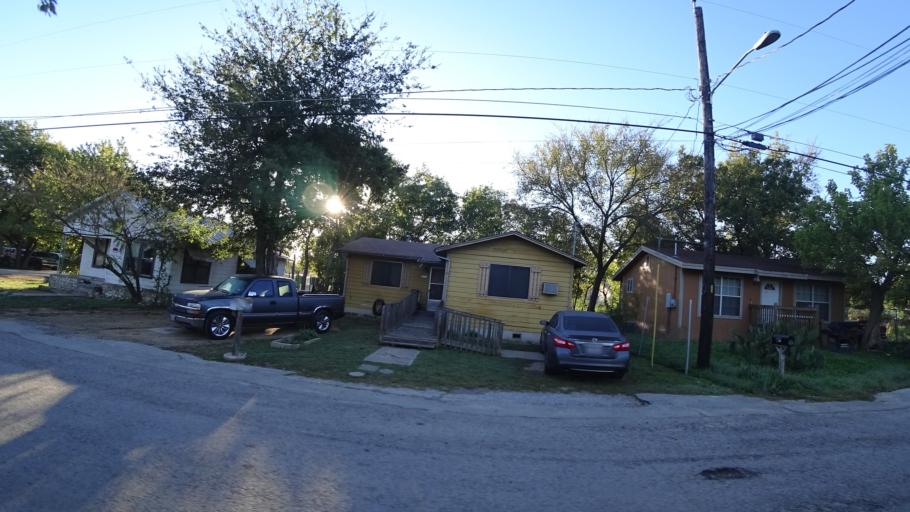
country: US
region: Texas
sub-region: Travis County
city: Hornsby Bend
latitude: 30.2047
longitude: -97.6379
